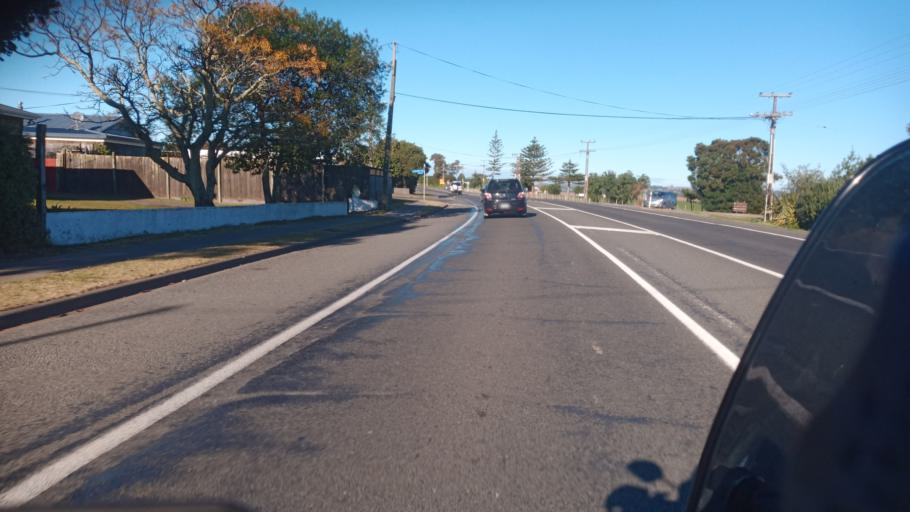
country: NZ
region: Hawke's Bay
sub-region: Napier City
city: Napier
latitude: -39.4345
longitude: 176.8705
